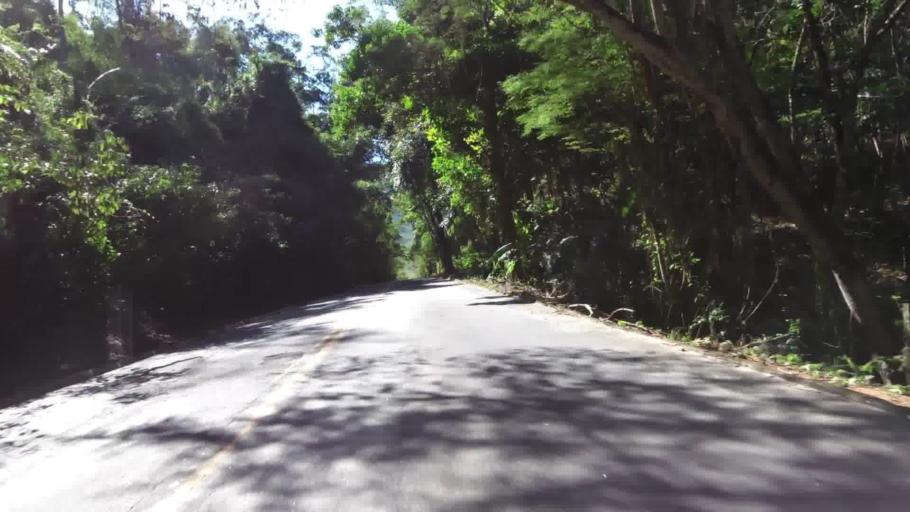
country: BR
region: Espirito Santo
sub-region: Rio Novo Do Sul
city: Rio Novo do Sul
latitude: -20.8701
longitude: -40.9068
